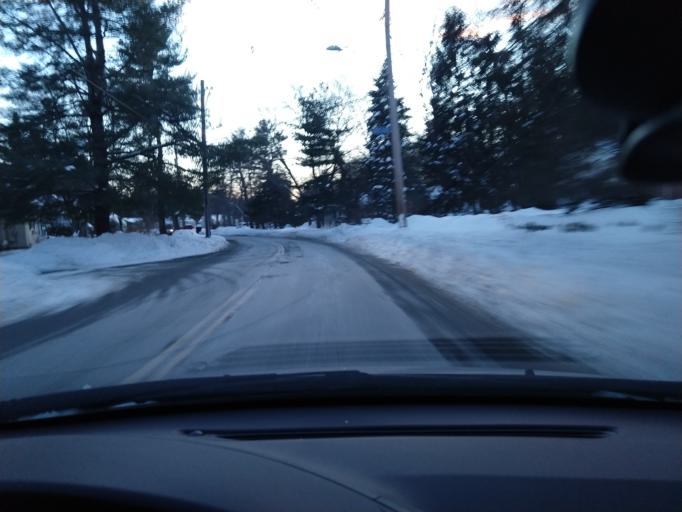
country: US
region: Massachusetts
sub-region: Middlesex County
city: Bedford
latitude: 42.4918
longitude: -71.2638
